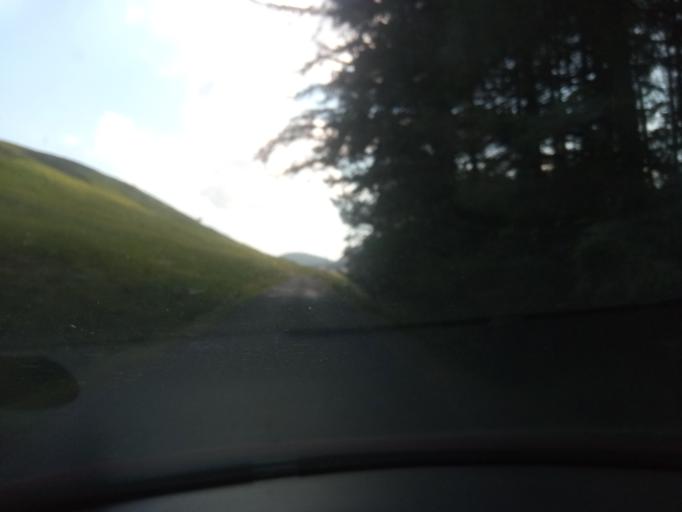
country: GB
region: Scotland
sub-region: The Scottish Borders
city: Innerleithen
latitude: 55.4923
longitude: -3.1214
